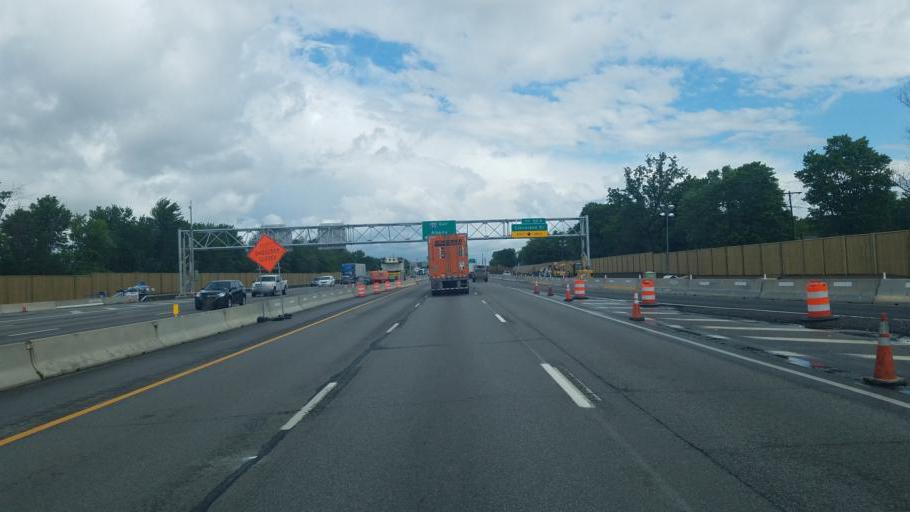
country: US
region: New York
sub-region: Erie County
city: Cheektowaga
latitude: 42.9355
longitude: -78.7662
